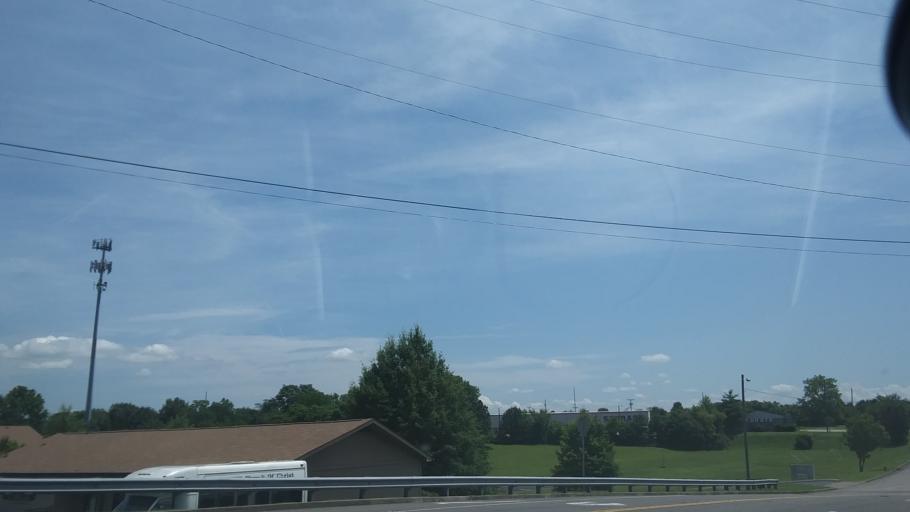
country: US
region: Tennessee
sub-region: Rutherford County
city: La Vergne
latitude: 36.0665
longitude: -86.6366
